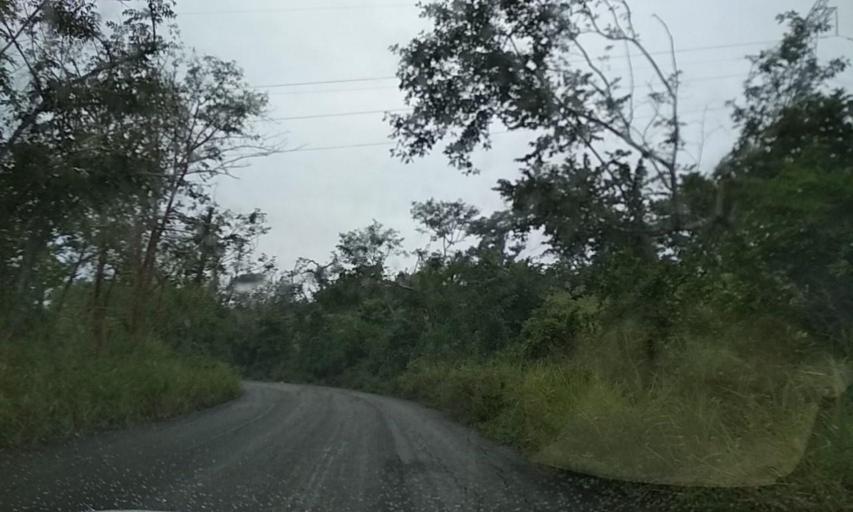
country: MX
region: Veracruz
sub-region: Coatzintla
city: Manuel Maria Contreras
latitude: 20.4565
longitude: -97.4733
